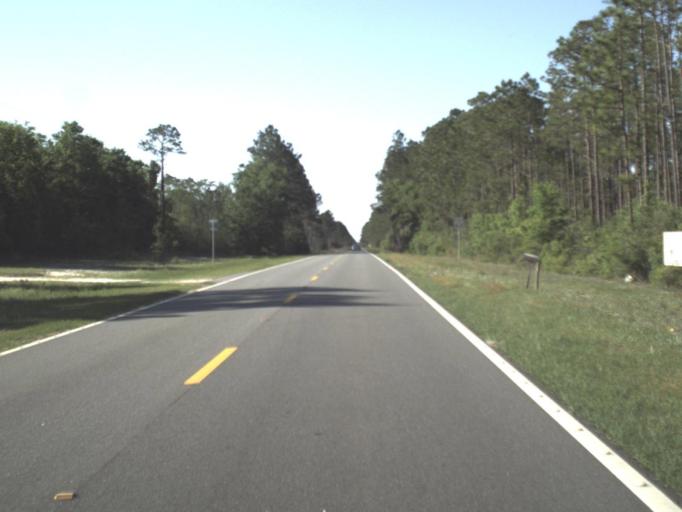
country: US
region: Florida
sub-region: Gulf County
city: Wewahitchka
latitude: 30.0341
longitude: -84.9836
